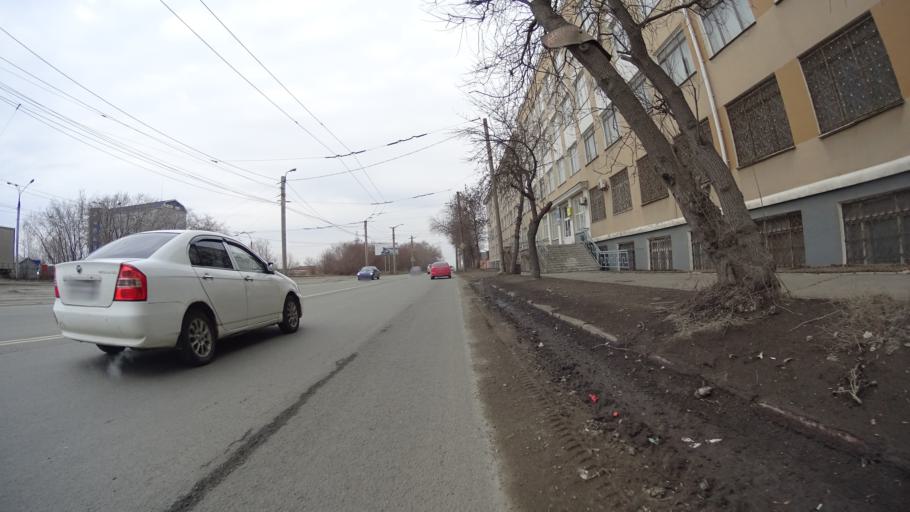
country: RU
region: Chelyabinsk
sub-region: Gorod Chelyabinsk
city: Chelyabinsk
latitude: 55.1589
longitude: 61.4707
